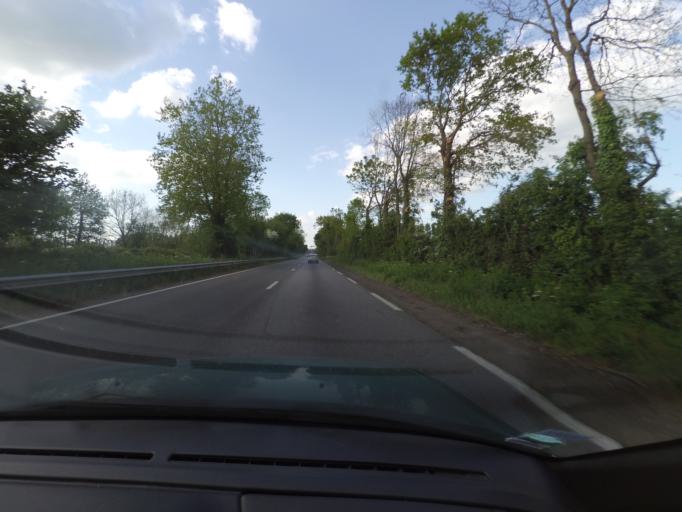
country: FR
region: Pays de la Loire
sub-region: Departement de la Vendee
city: Belleville-sur-Vie
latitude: 46.7613
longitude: -1.4307
